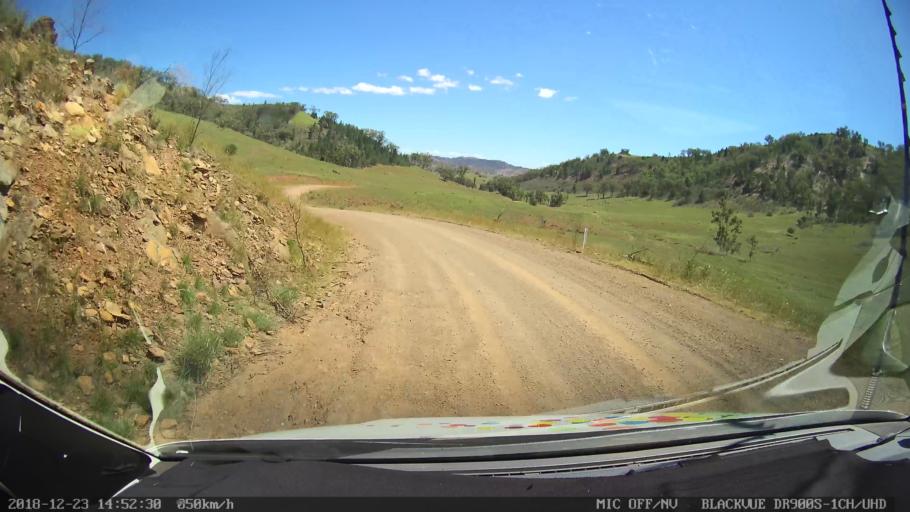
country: AU
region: New South Wales
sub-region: Tamworth Municipality
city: Manilla
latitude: -30.6847
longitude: 150.8542
